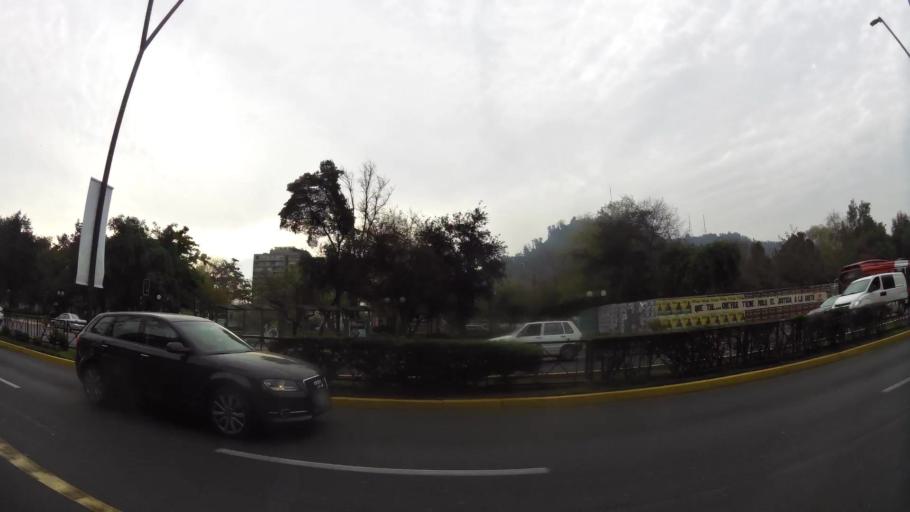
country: CL
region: Santiago Metropolitan
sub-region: Provincia de Santiago
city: Santiago
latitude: -33.4360
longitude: -70.6306
